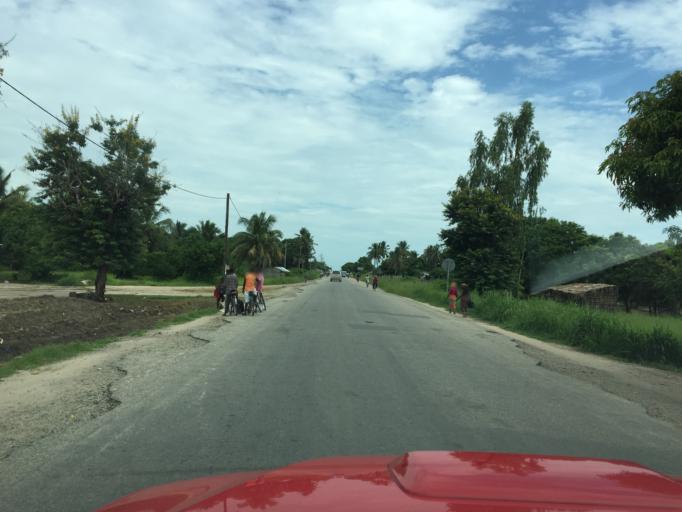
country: MZ
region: Zambezia
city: Quelimane
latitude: -17.5991
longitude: 36.8176
